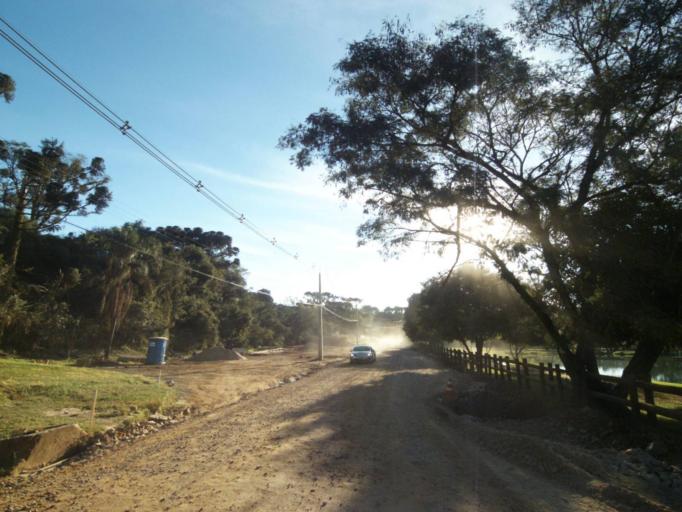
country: BR
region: Parana
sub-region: Tibagi
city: Tibagi
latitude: -24.5196
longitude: -50.4199
